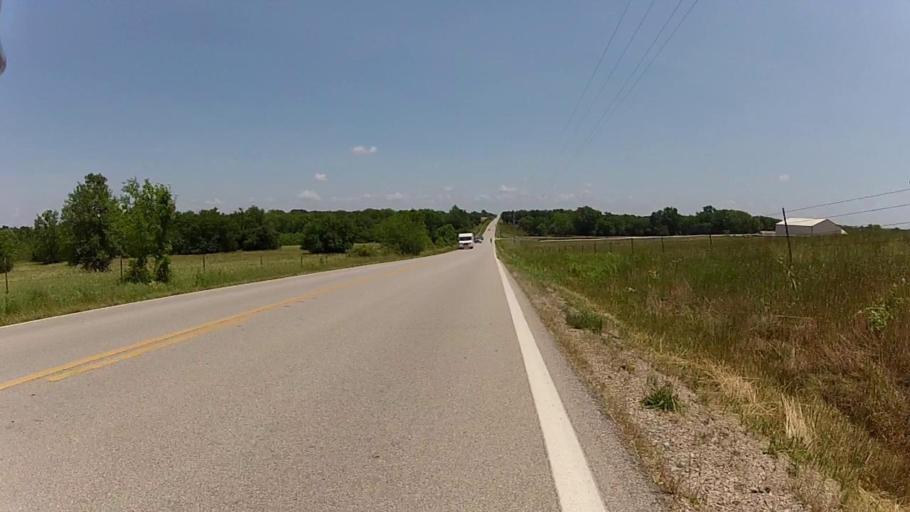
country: US
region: Kansas
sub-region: Montgomery County
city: Cherryvale
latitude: 37.1937
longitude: -95.5178
